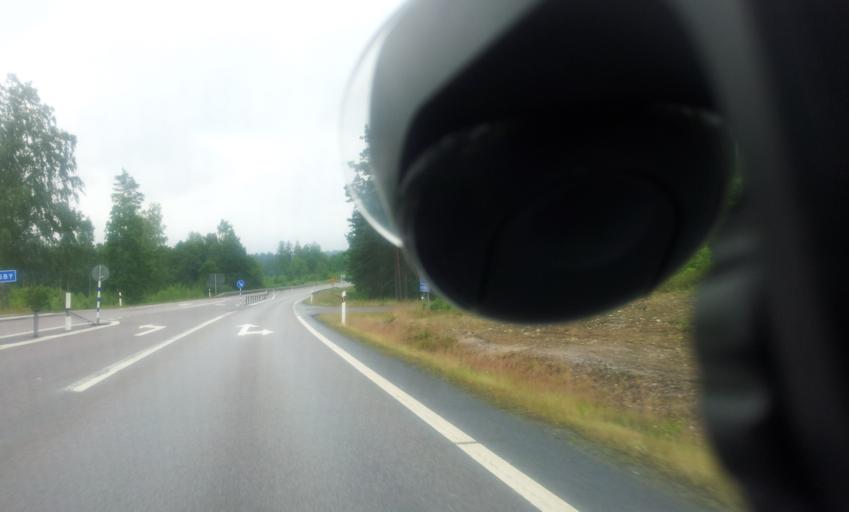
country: SE
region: Kalmar
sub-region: Vasterviks Kommun
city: Forserum
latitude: 58.0587
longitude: 16.5292
